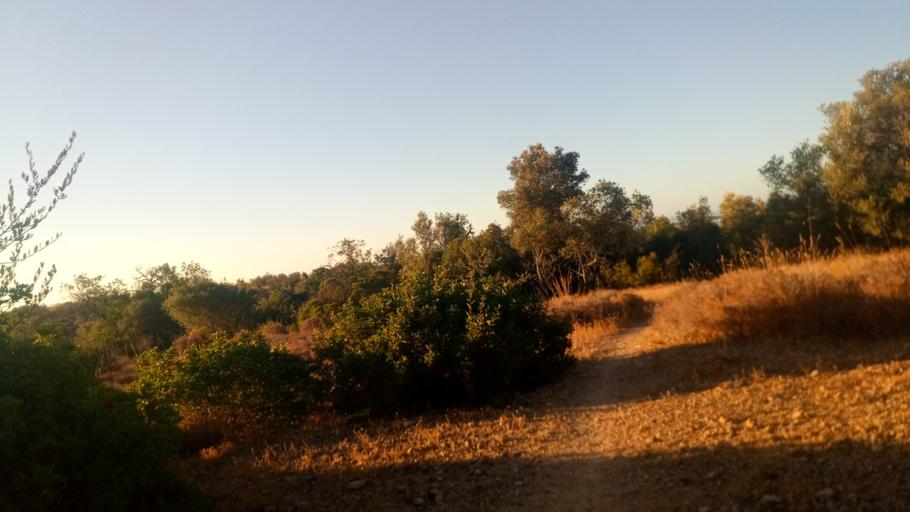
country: PT
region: Faro
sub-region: Tavira
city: Tavira
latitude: 37.1412
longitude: -7.6126
